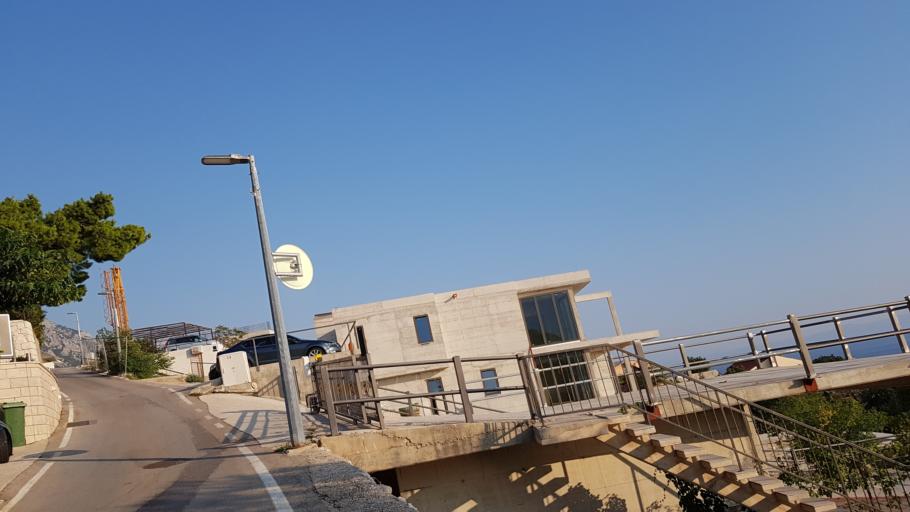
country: HR
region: Splitsko-Dalmatinska
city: Donja Brela
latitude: 43.3851
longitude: 16.9060
